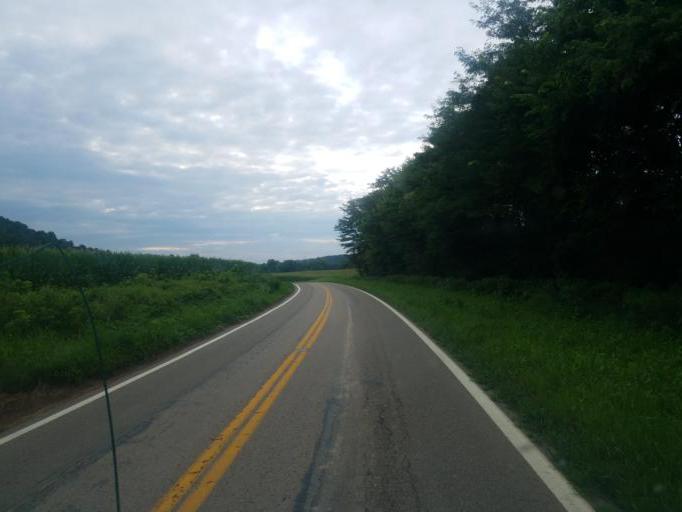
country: US
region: Ohio
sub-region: Knox County
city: Oak Hill
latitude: 40.3542
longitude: -82.1237
